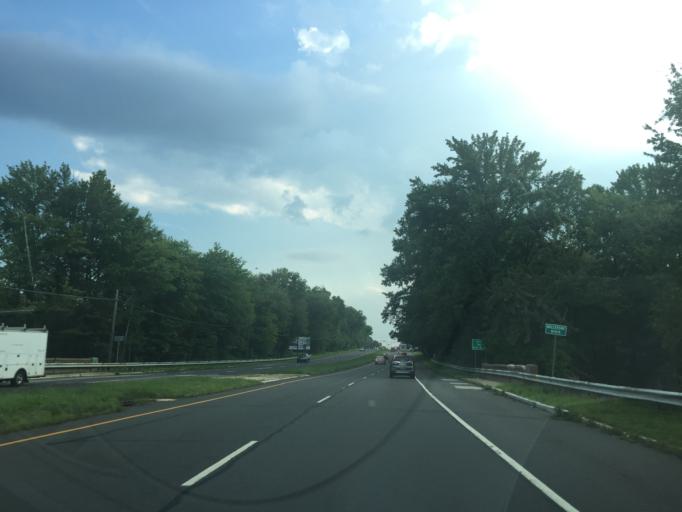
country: US
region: New Jersey
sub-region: Mercer County
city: Hightstown
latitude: 40.2908
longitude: -74.5216
